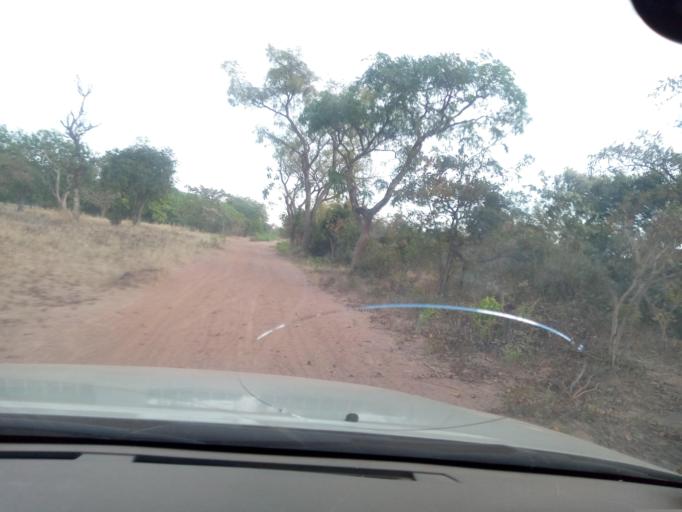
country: ML
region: Sikasso
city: Kadiolo
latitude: 10.5972
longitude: -5.8829
